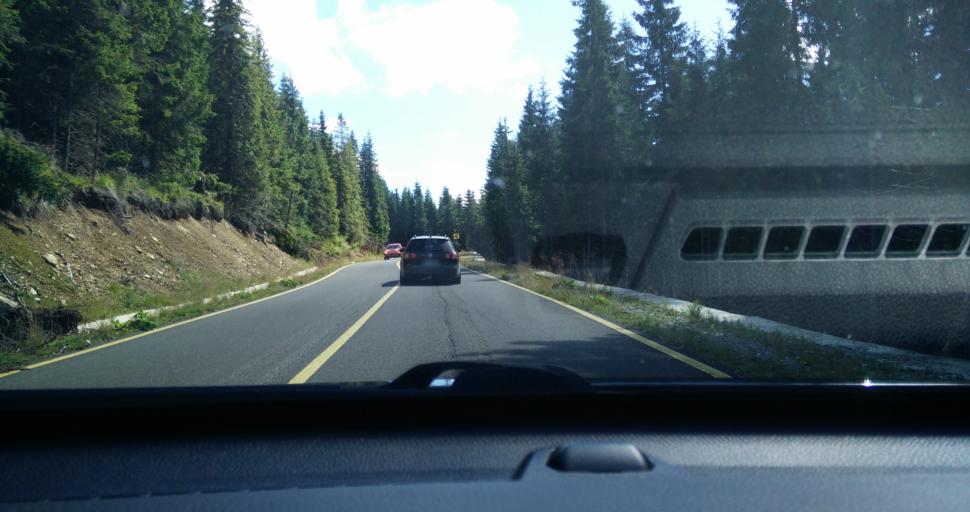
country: RO
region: Hunedoara
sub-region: Oras Petrila
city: Petrila
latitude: 45.4662
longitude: 23.6263
